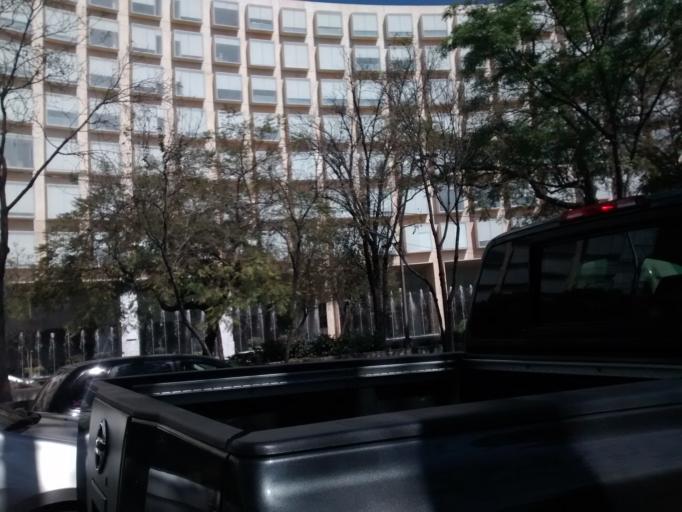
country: MX
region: Mexico City
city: Miguel Hidalgo
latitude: 19.4383
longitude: -99.2025
